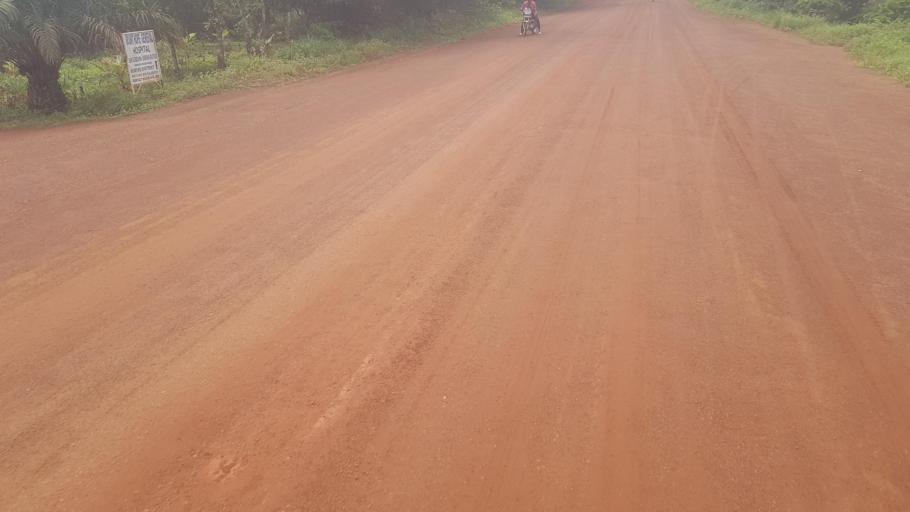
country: SL
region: Southern Province
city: Mogbwemo
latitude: 7.7497
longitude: -12.3058
